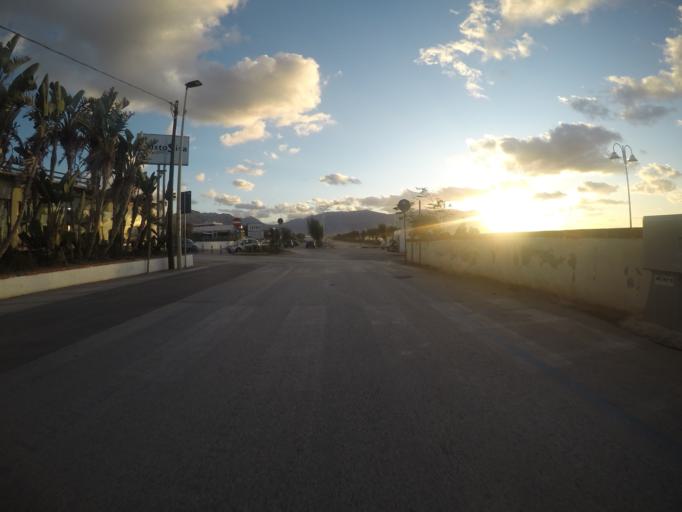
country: IT
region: Sicily
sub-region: Palermo
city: Isola delle Femmine
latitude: 38.1857
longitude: 13.2380
